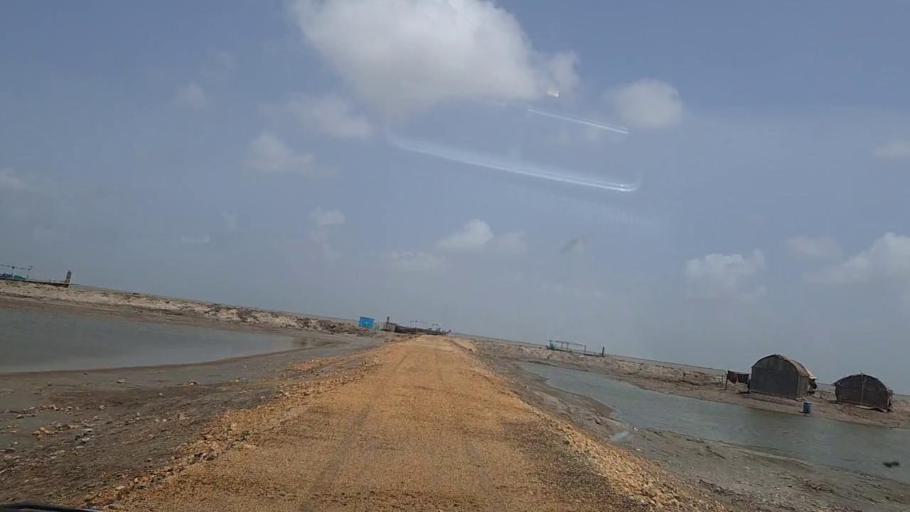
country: PK
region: Sindh
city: Keti Bandar
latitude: 24.1272
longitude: 67.4686
